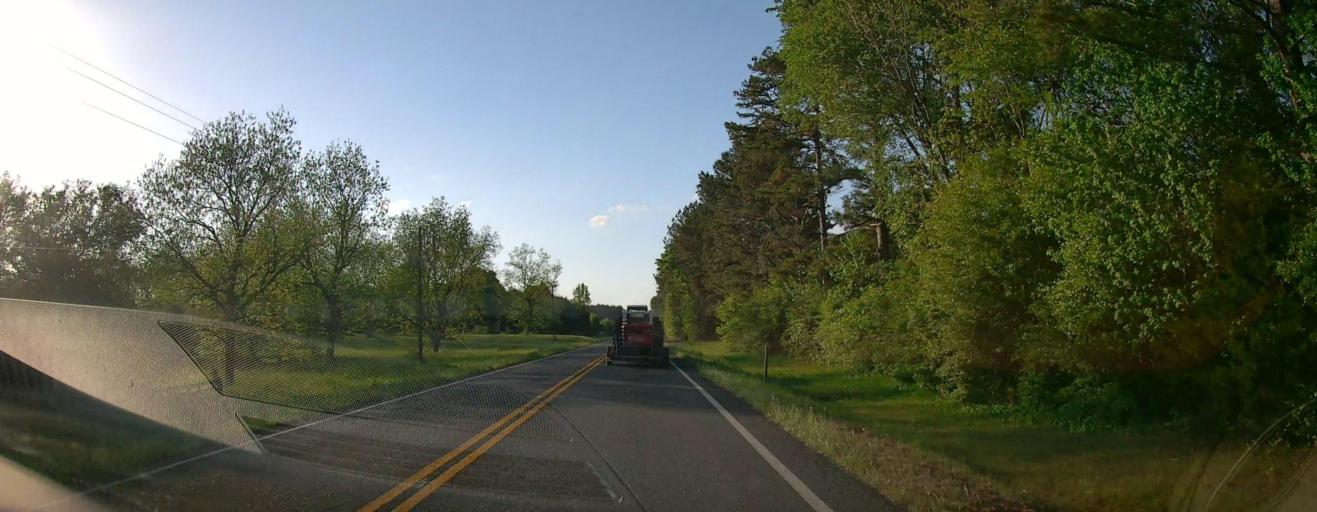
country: US
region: Georgia
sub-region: Jasper County
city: Monticello
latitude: 33.4206
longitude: -83.6128
